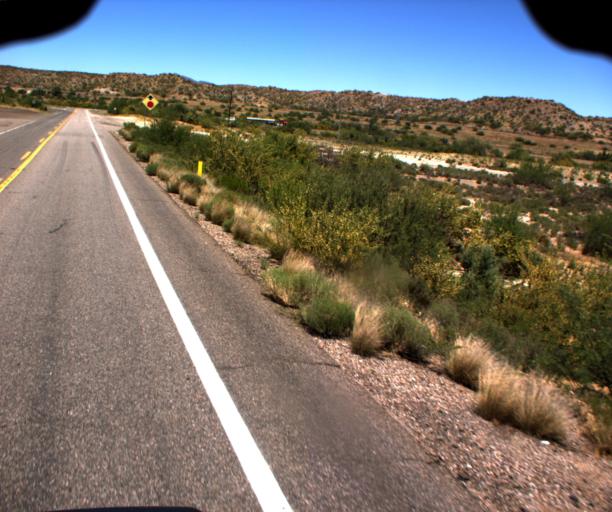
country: US
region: Arizona
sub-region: Gila County
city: Globe
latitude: 33.3708
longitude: -110.7378
